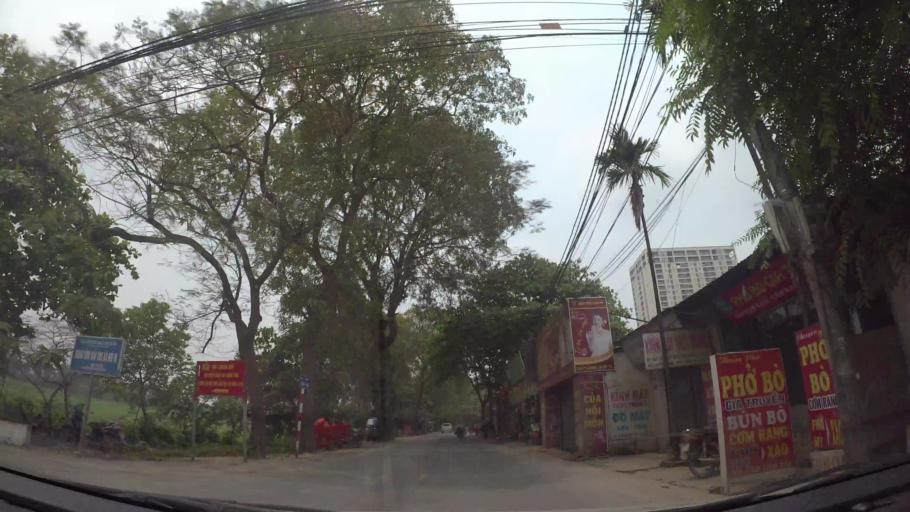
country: VN
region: Ha Noi
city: Cau Dien
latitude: 21.0148
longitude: 105.7458
